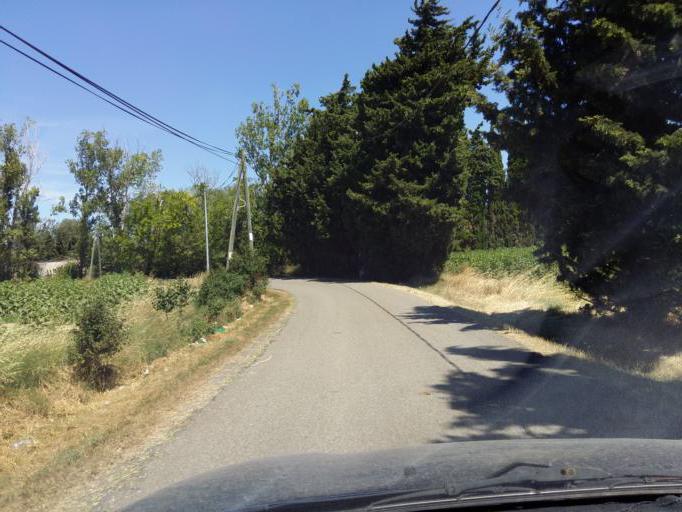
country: FR
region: Provence-Alpes-Cote d'Azur
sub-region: Departement du Vaucluse
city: Piolenc
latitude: 44.1710
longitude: 4.7524
